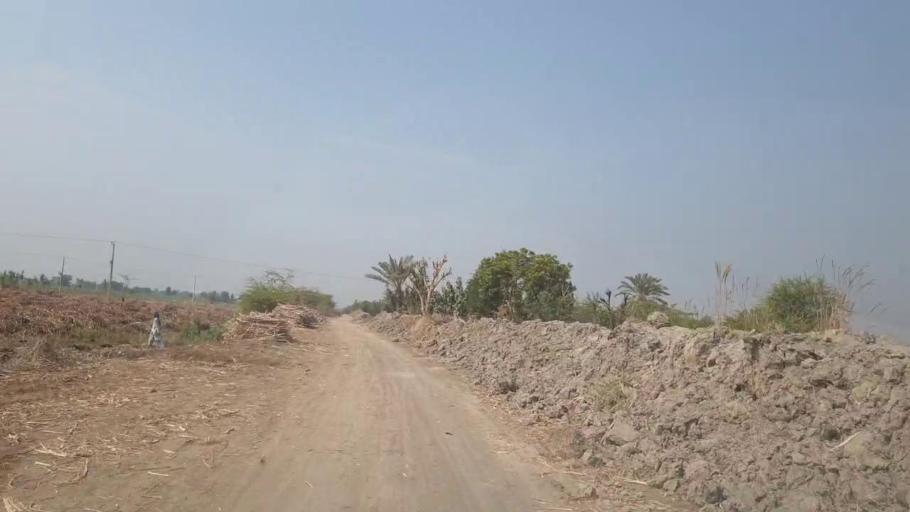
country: PK
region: Sindh
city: Mirpur Khas
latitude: 25.5672
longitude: 69.1430
